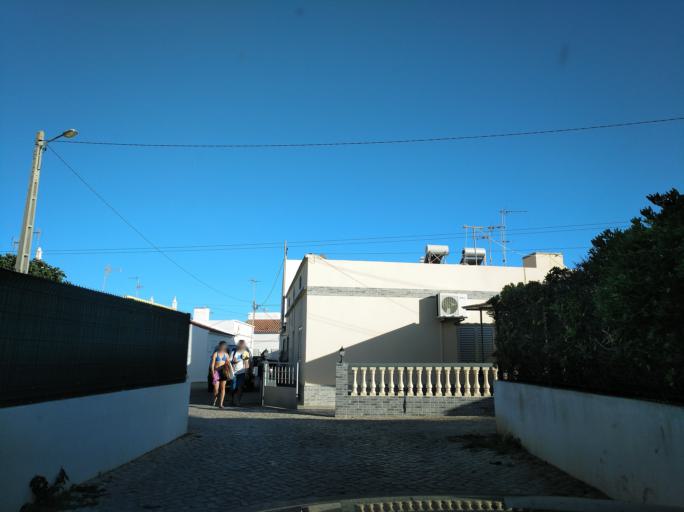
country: PT
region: Faro
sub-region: Vila Real de Santo Antonio
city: Monte Gordo
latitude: 37.1758
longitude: -7.4979
